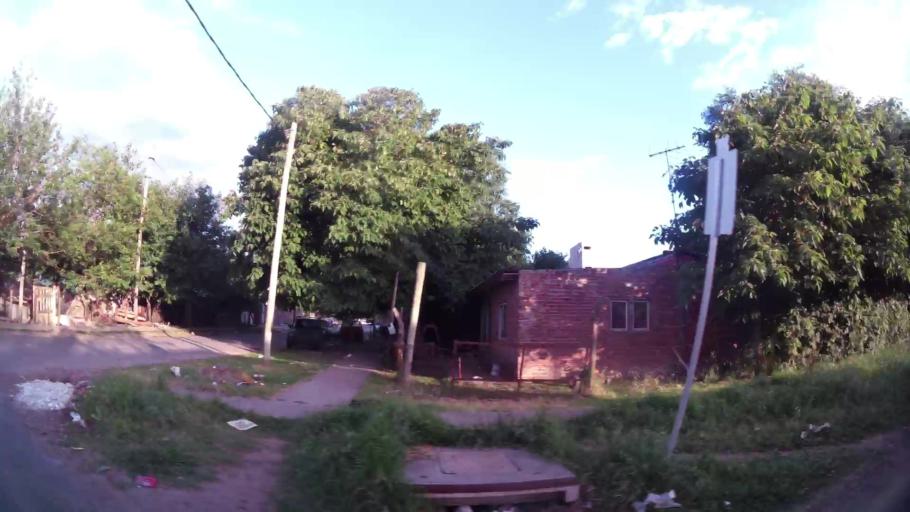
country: AR
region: Buenos Aires
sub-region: Partido de Tigre
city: Tigre
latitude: -34.4493
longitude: -58.6551
